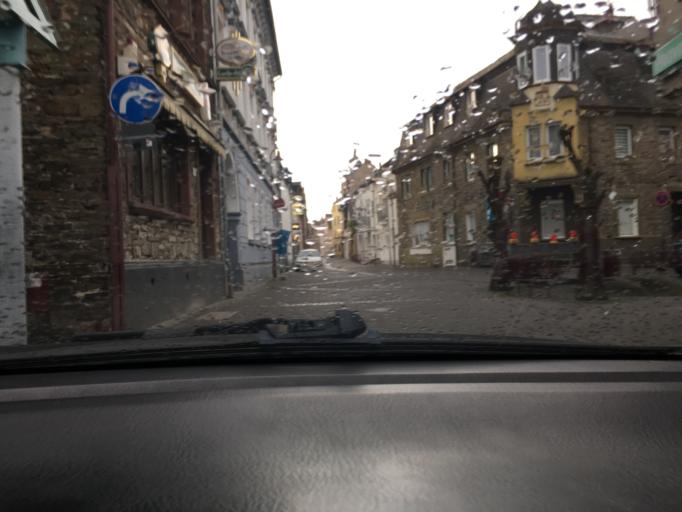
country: DE
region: Rheinland-Pfalz
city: Bendorf
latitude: 50.4214
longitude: 7.5752
